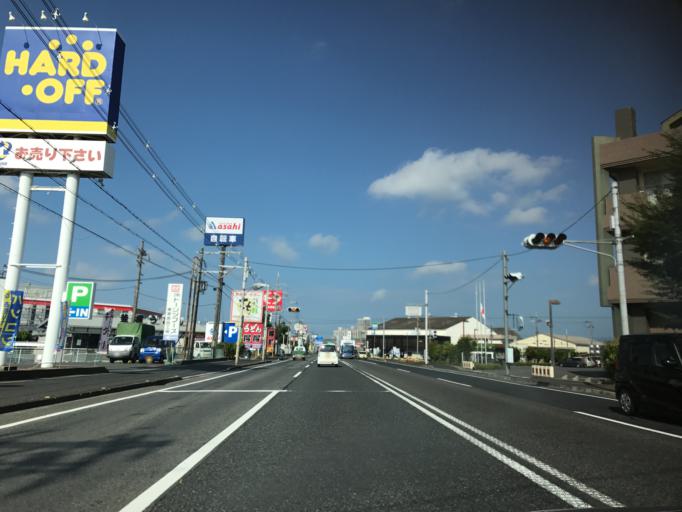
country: JP
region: Shiga Prefecture
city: Kusatsu
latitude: 35.0222
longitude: 135.9806
